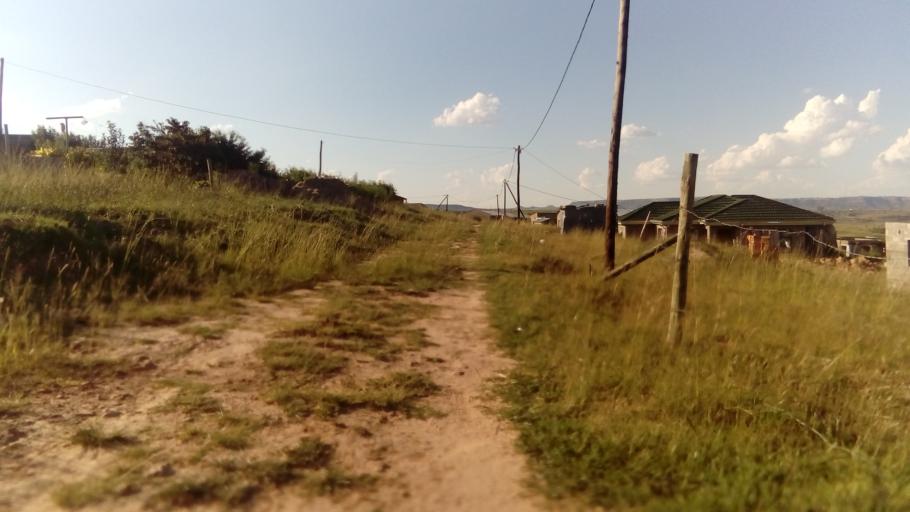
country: LS
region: Berea
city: Teyateyaneng
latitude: -29.1319
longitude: 27.7631
